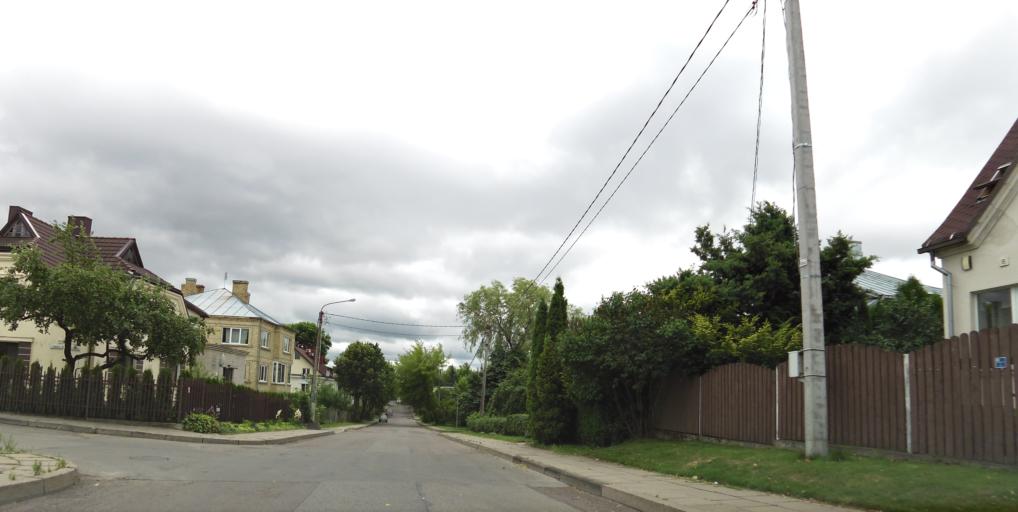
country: LT
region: Vilnius County
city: Seskine
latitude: 54.6964
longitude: 25.2457
